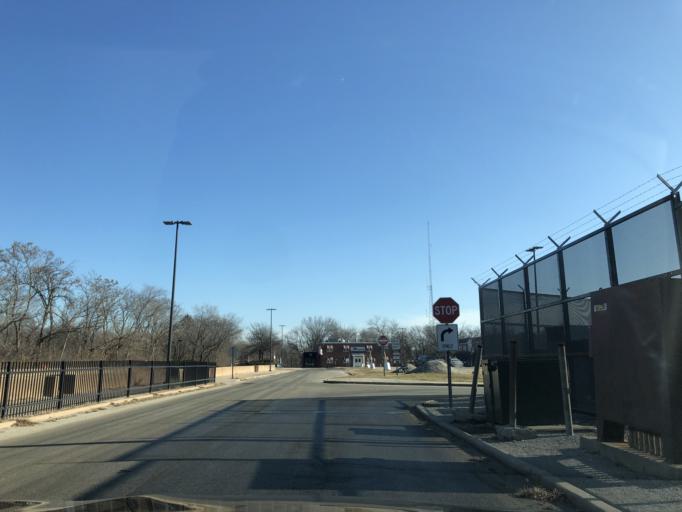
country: US
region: Illinois
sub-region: Cook County
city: Forest Park
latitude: 41.8752
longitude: -87.8279
